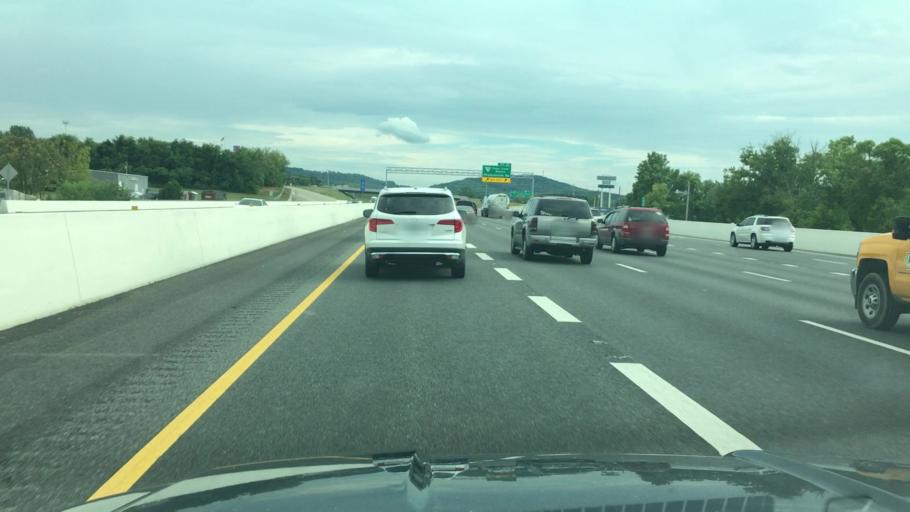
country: US
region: Tennessee
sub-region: Williamson County
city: Franklin
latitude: 35.8650
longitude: -86.8316
